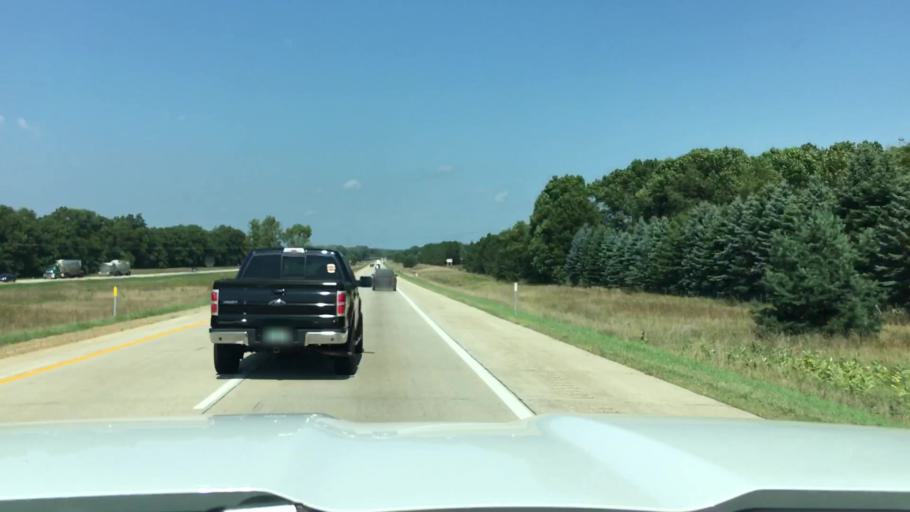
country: US
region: Michigan
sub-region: Allegan County
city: Plainwell
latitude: 42.3897
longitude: -85.6593
